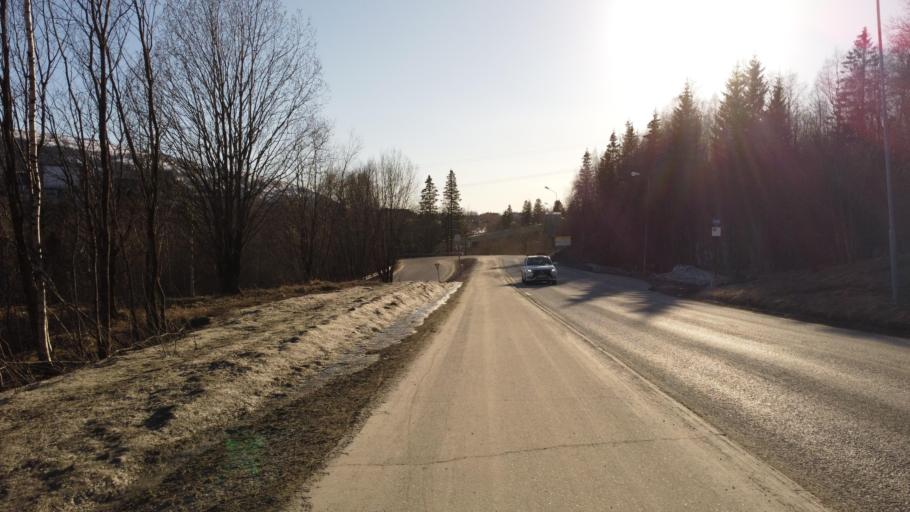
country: NO
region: Nordland
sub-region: Rana
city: Mo i Rana
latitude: 66.3181
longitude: 14.1779
